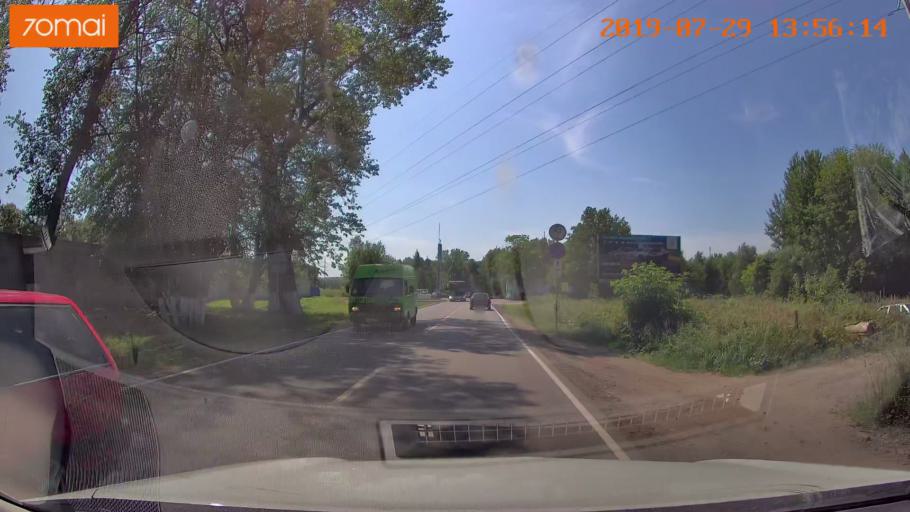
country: RU
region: Kaliningrad
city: Primorsk
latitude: 54.7095
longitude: 19.9506
